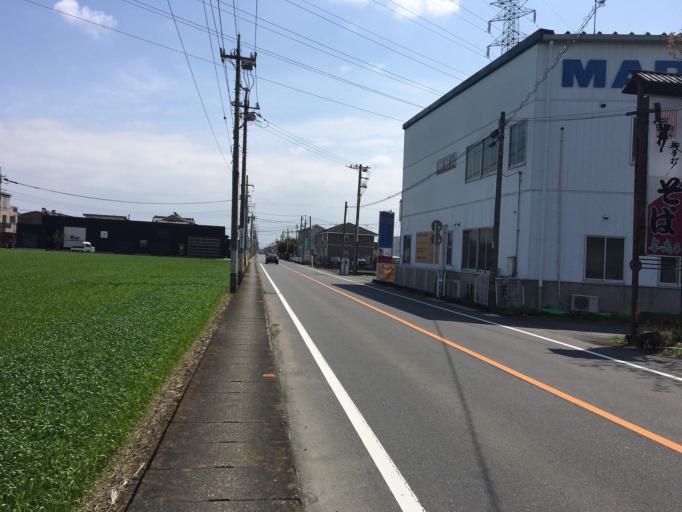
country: JP
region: Gunma
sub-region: Sawa-gun
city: Tamamura
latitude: 36.3035
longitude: 139.0964
